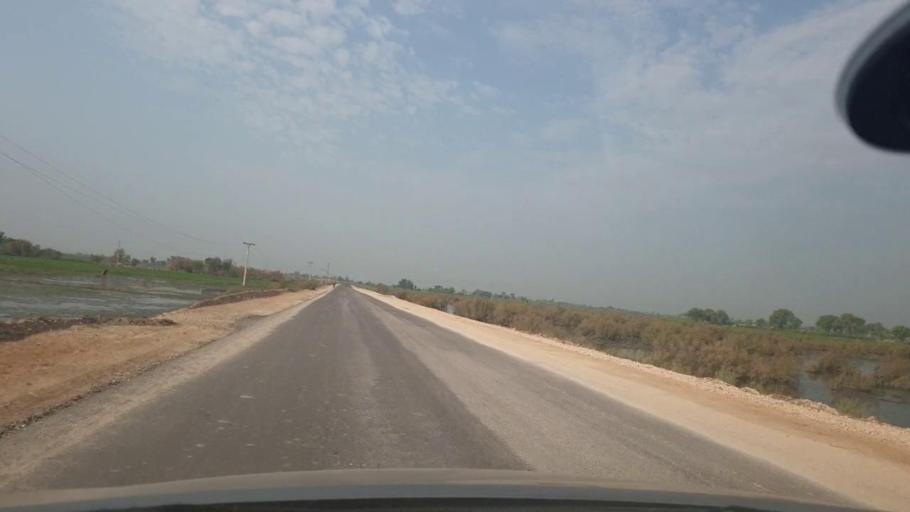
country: PK
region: Sindh
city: Jacobabad
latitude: 28.1354
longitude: 68.3371
